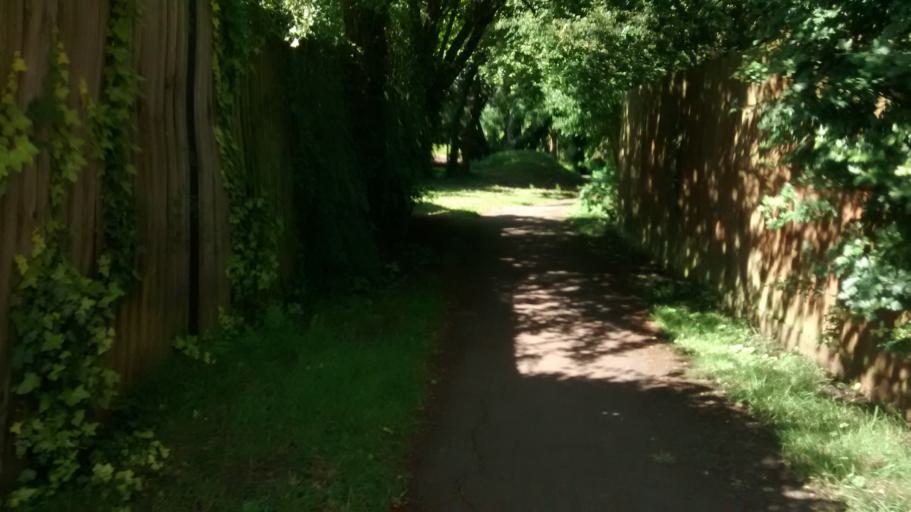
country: GB
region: England
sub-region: Cambridgeshire
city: Grantchester
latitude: 52.2000
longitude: 0.0958
